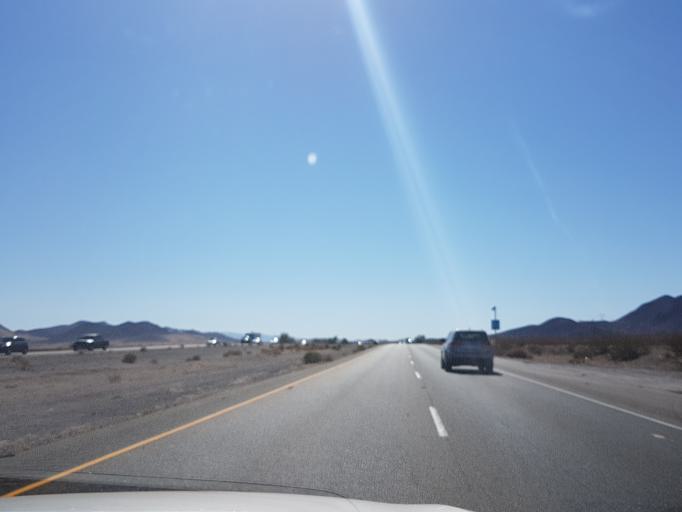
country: US
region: California
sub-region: San Bernardino County
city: Fort Irwin
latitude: 35.1670
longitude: -116.1812
